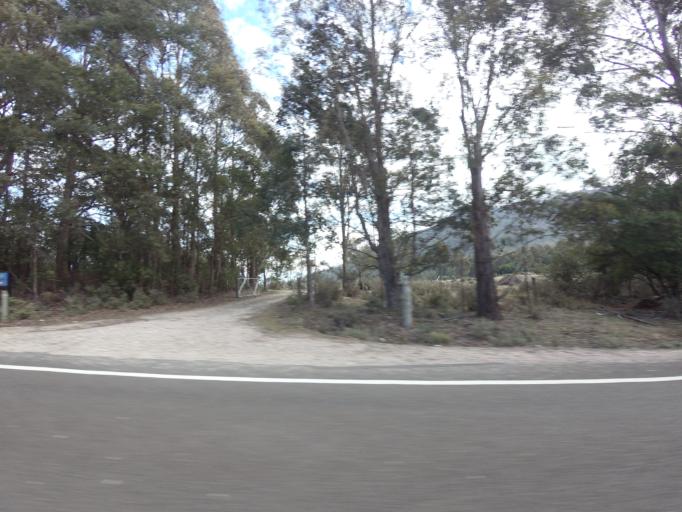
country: AU
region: Tasmania
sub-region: Meander Valley
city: Deloraine
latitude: -41.6594
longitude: 146.7230
